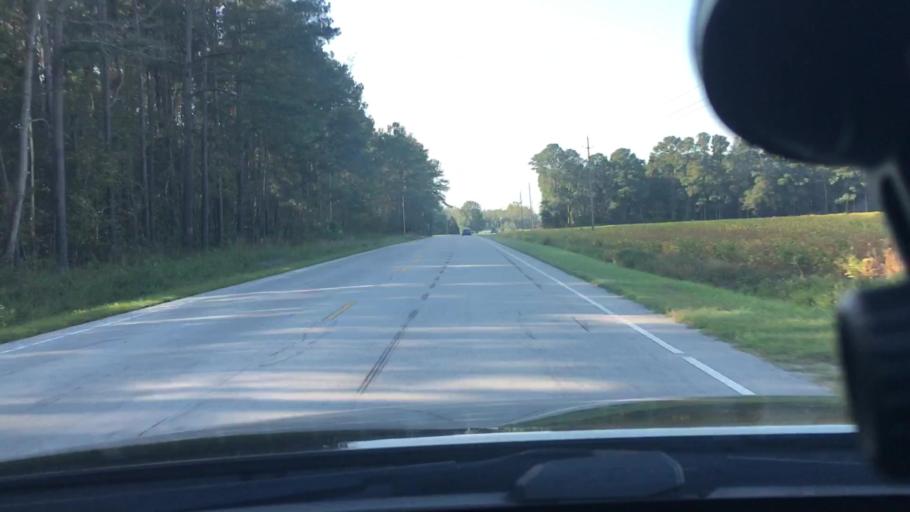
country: US
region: North Carolina
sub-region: Pitt County
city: Windsor
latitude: 35.4814
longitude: -77.2997
